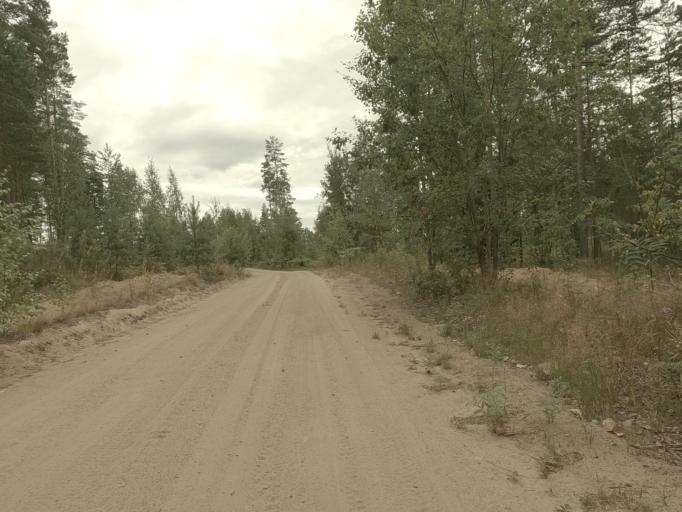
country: RU
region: Leningrad
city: Kamennogorsk
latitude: 61.0016
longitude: 29.1797
